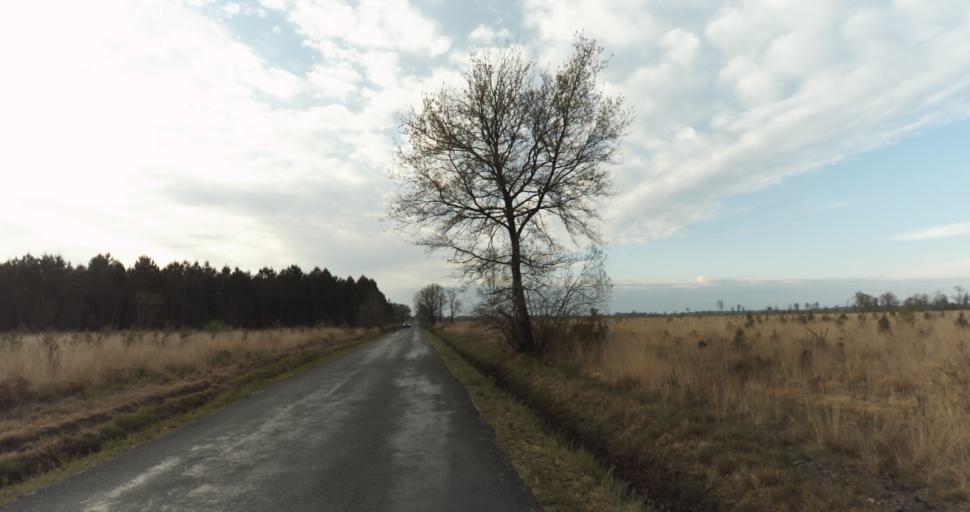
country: FR
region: Aquitaine
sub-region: Departement de la Gironde
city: Saint-Aubin-de-Medoc
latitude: 44.7870
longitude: -0.7534
